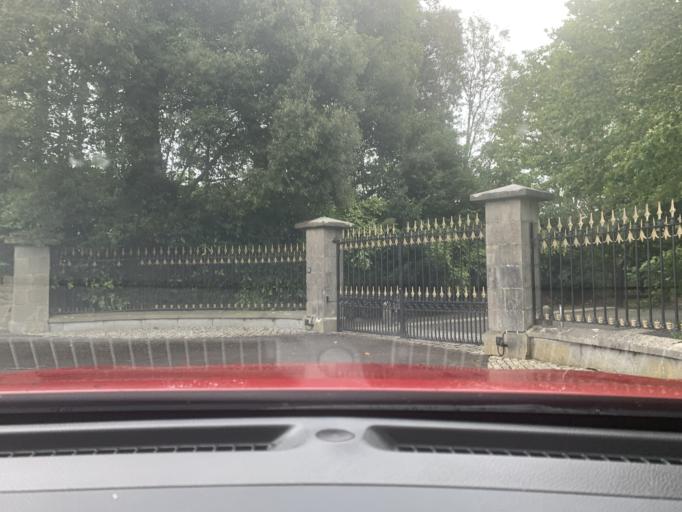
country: IE
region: Connaught
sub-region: Sligo
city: Strandhill
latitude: 54.2194
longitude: -8.6212
